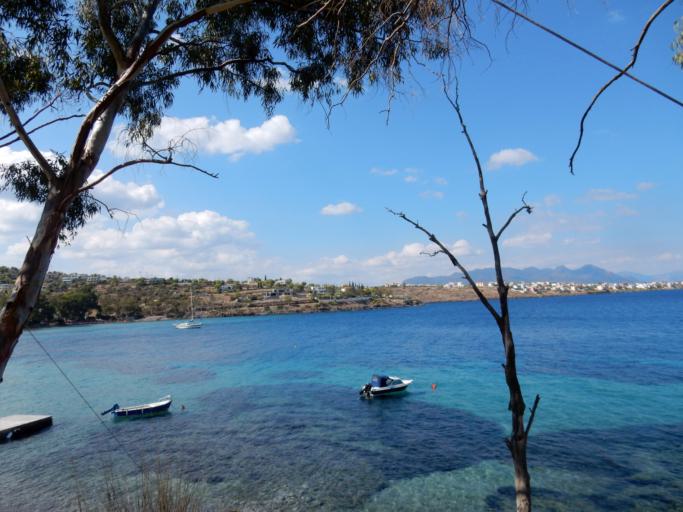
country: GR
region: Attica
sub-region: Nomos Piraios
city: Kypseli
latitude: 37.7015
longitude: 23.4675
